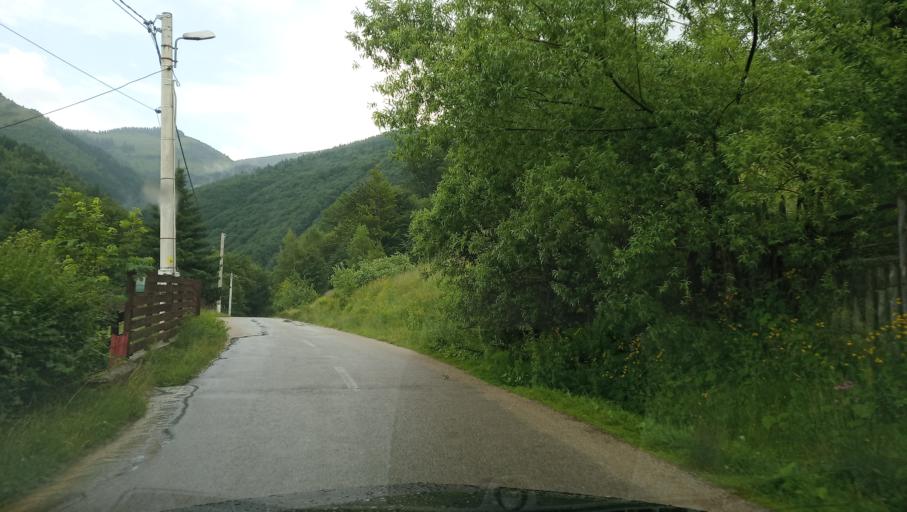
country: RO
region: Hunedoara
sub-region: Oras Petrila
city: Petrila
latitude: 45.3924
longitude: 23.4389
